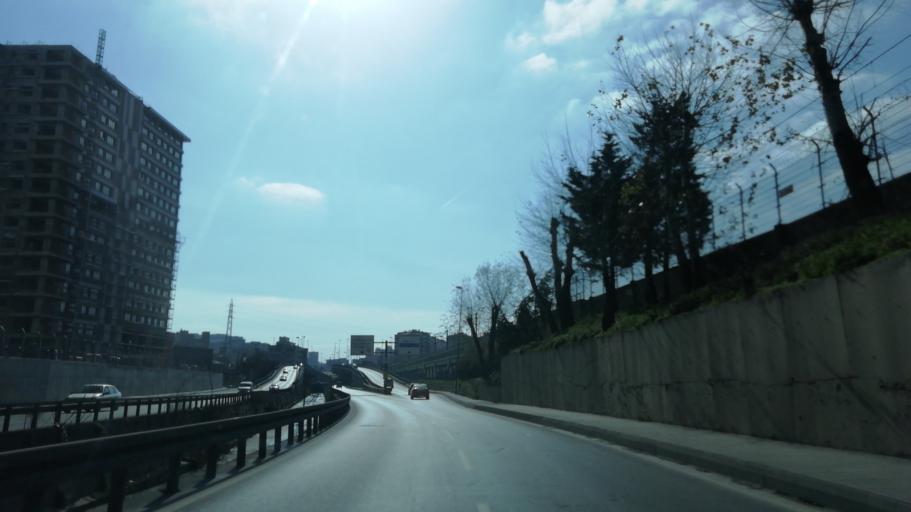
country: TR
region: Istanbul
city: merter keresteciler
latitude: 41.0238
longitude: 28.8993
